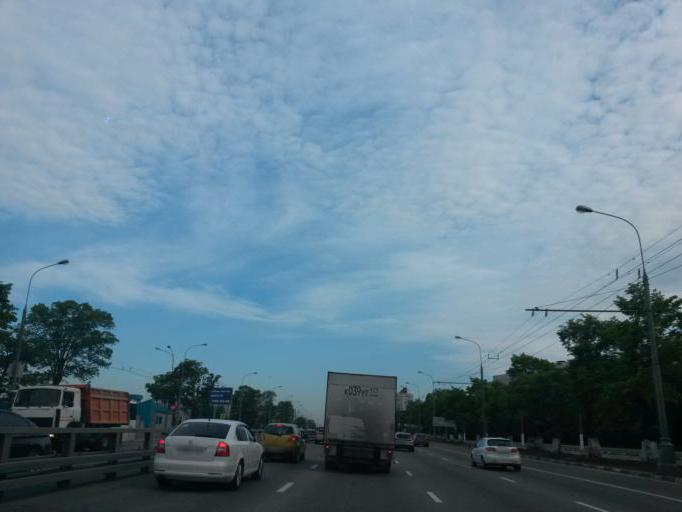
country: RU
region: Moscow
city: Orekhovo-Borisovo
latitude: 55.6047
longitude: 37.7206
